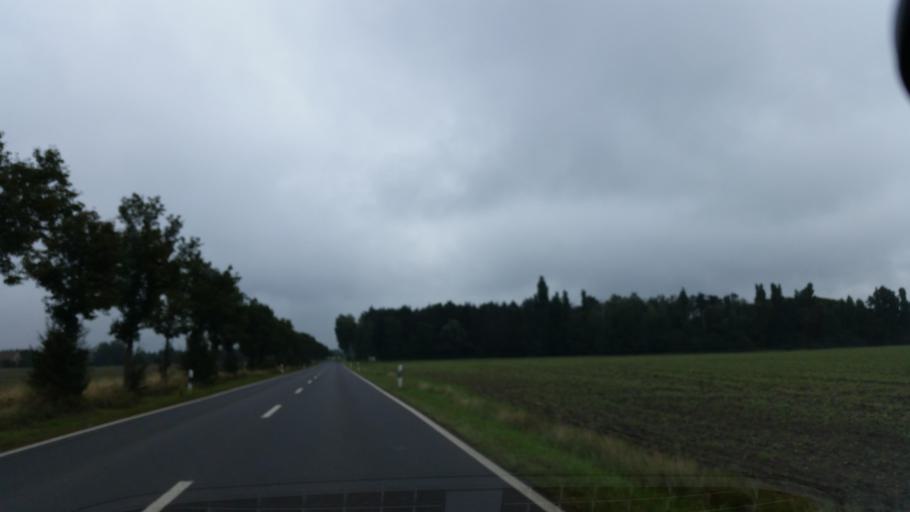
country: DE
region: Saxony
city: Bad Muskau
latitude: 51.5431
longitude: 14.6902
